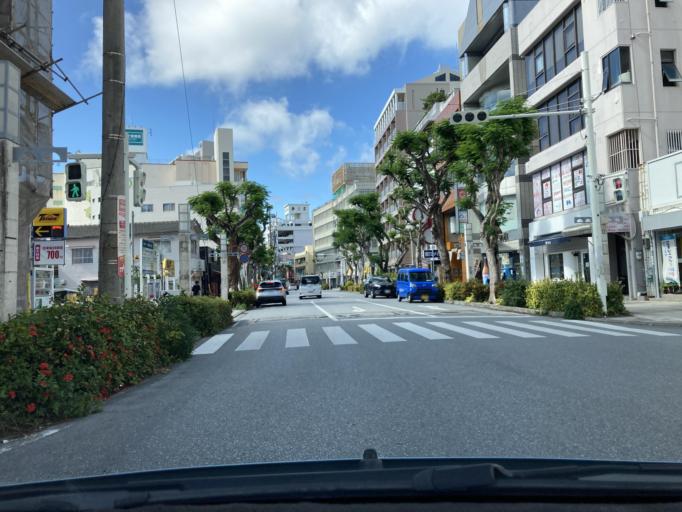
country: JP
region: Okinawa
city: Naha-shi
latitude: 26.2179
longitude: 127.6871
